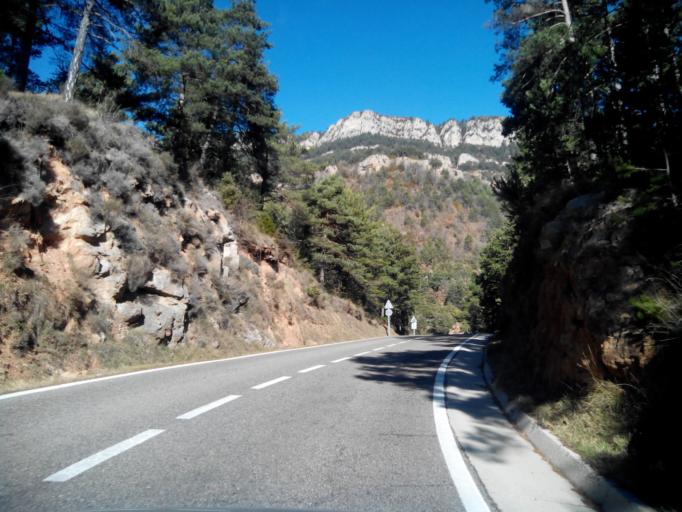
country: ES
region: Catalonia
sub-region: Provincia de Barcelona
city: Capolat
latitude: 42.0896
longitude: 1.7811
